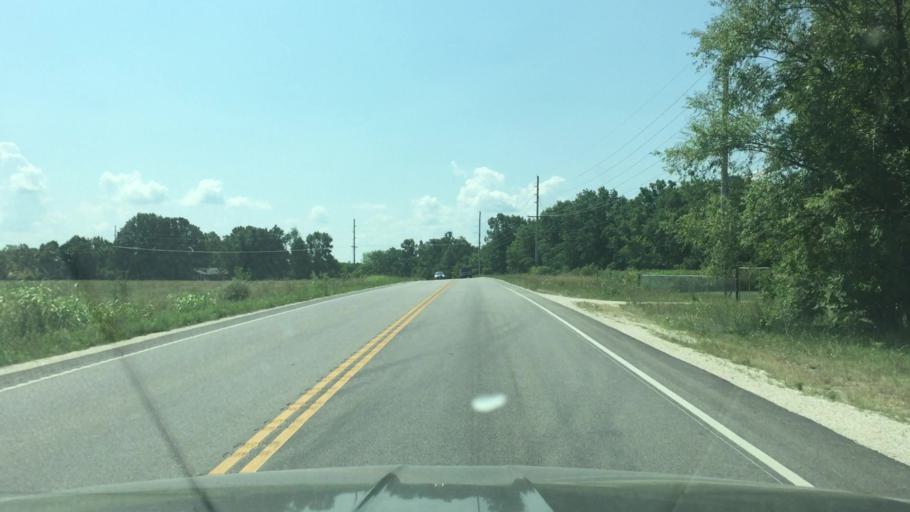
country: US
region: Missouri
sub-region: Miller County
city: Eldon
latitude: 38.3679
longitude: -92.6157
